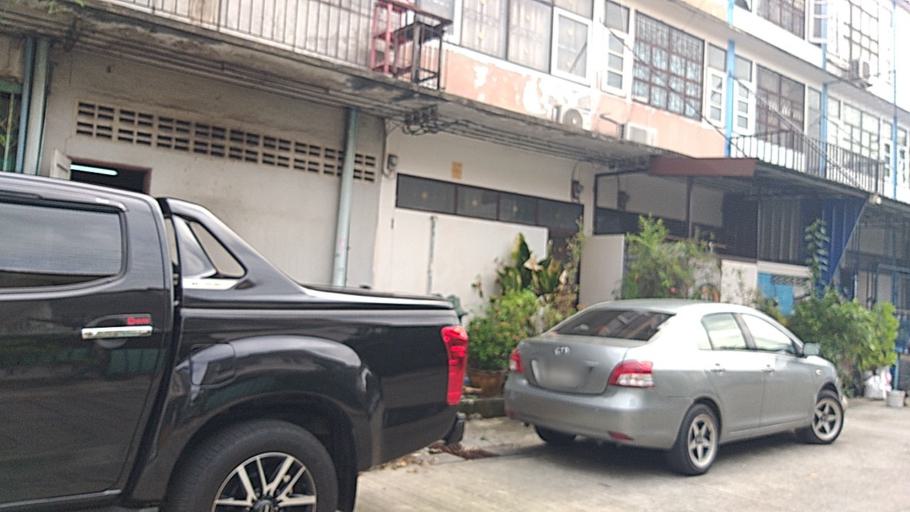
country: TH
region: Bangkok
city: Suan Luang
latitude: 13.7106
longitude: 100.6626
